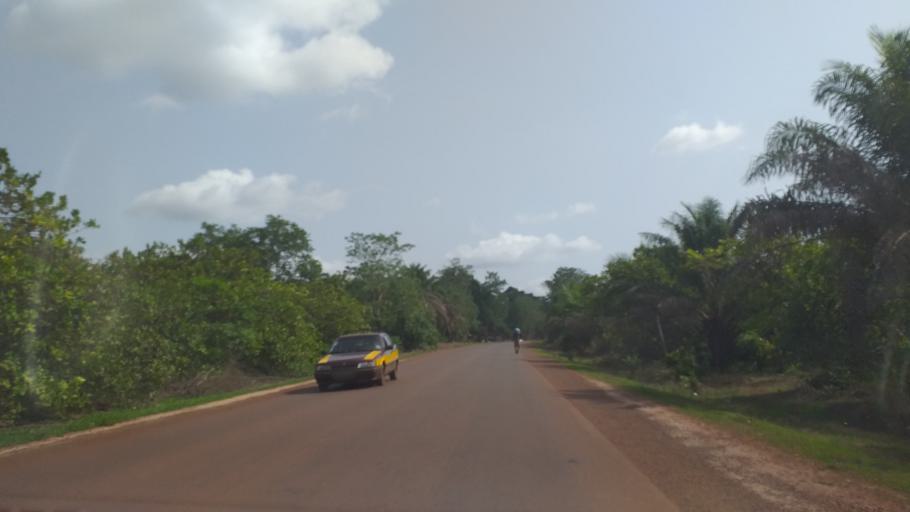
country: GN
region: Boke
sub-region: Boke Prefecture
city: Sangueya
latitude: 10.8230
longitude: -14.3727
